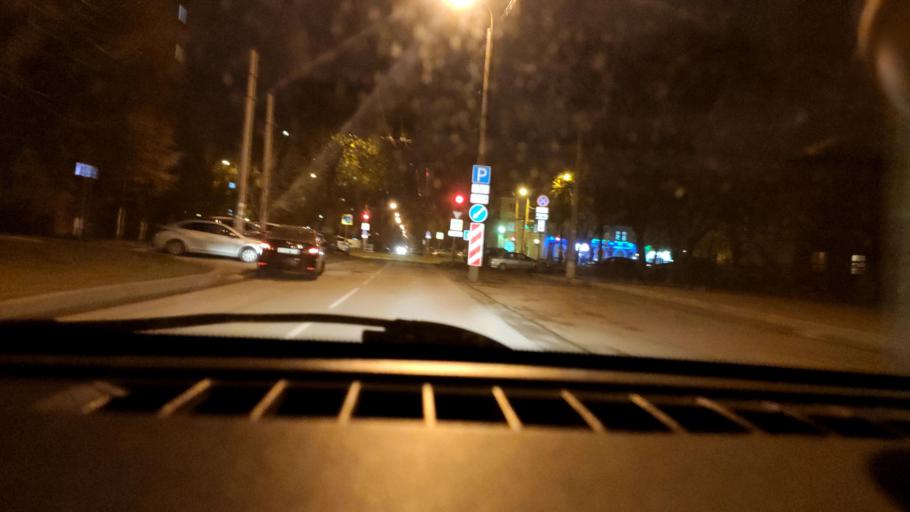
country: RU
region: Samara
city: Samara
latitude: 53.2201
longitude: 50.2481
